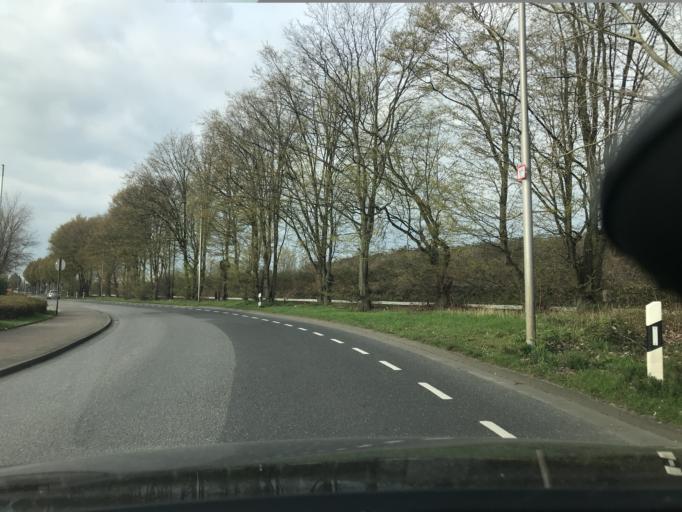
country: DE
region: North Rhine-Westphalia
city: Kempen
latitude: 51.3739
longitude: 6.4205
